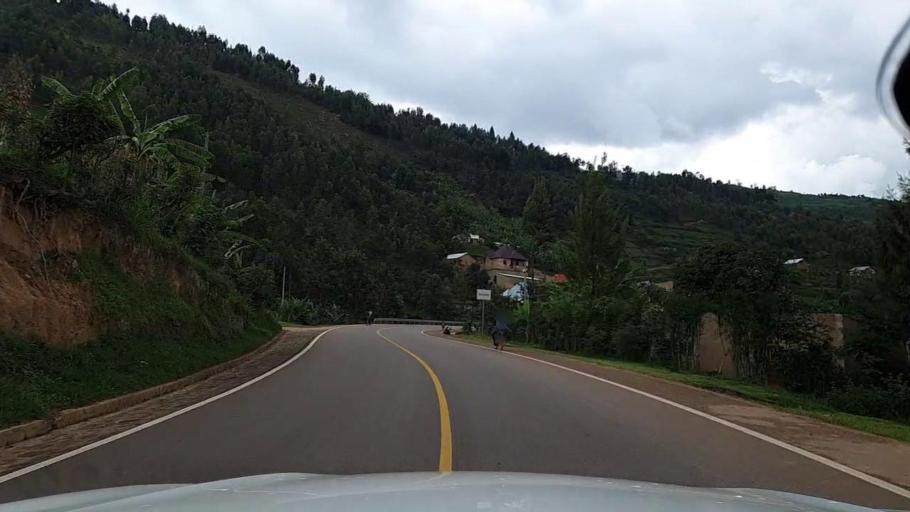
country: RW
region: Northern Province
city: Byumba
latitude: -1.6757
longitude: 30.0947
